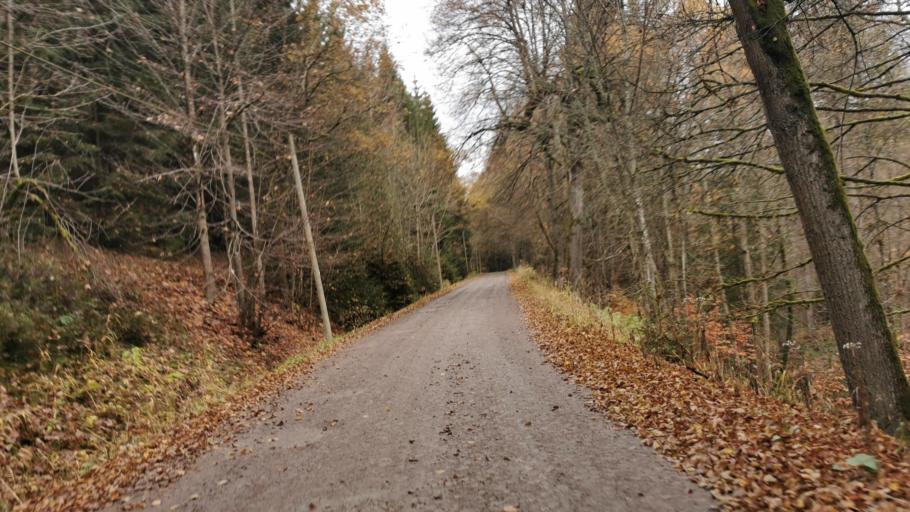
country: DE
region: Thuringia
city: Wurzbach
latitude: 50.4479
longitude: 11.5478
